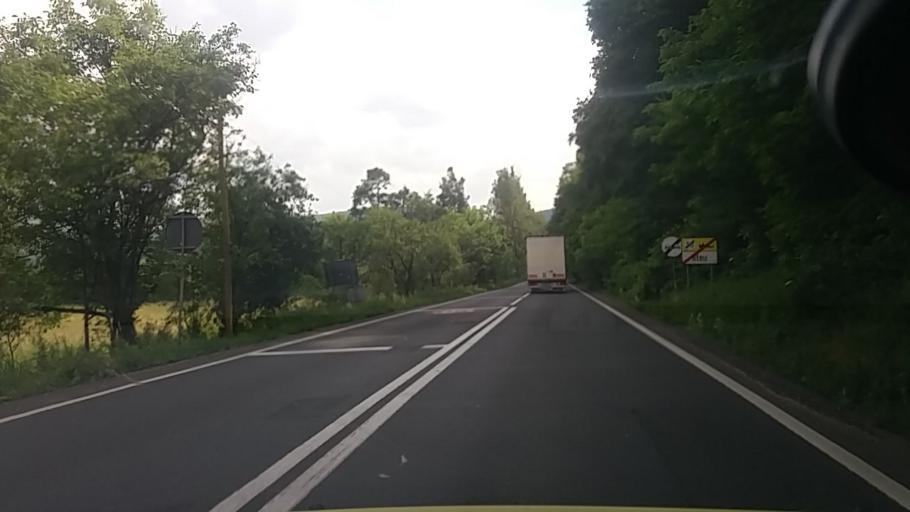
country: RO
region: Arad
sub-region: Comuna Petris
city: Petris
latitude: 46.0129
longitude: 22.3460
